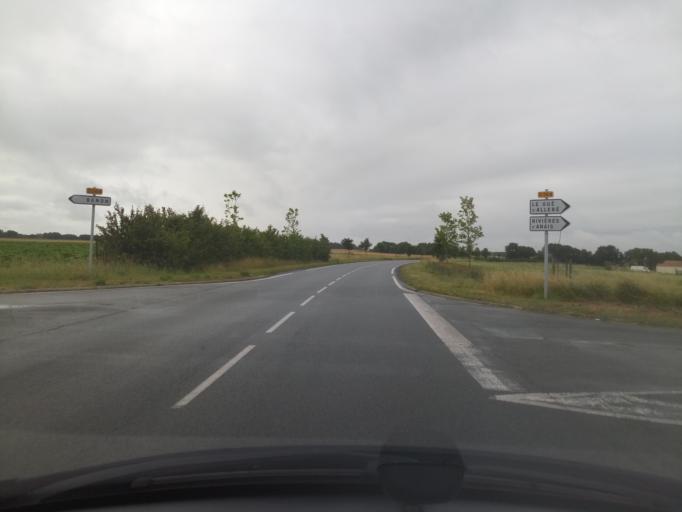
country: FR
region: Poitou-Charentes
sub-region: Departement de la Charente-Maritime
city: Courcon
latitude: 46.1876
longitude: -0.8548
